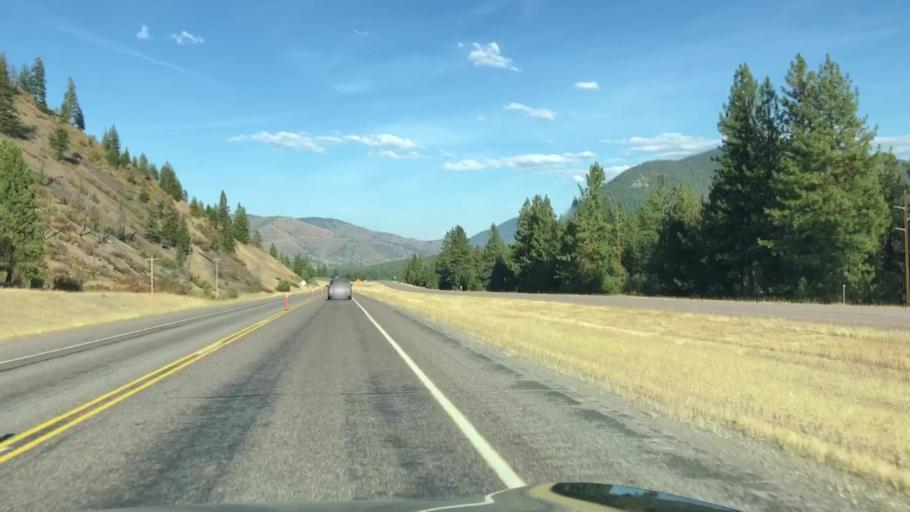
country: US
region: Montana
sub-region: Mineral County
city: Superior
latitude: 47.0123
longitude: -114.7082
